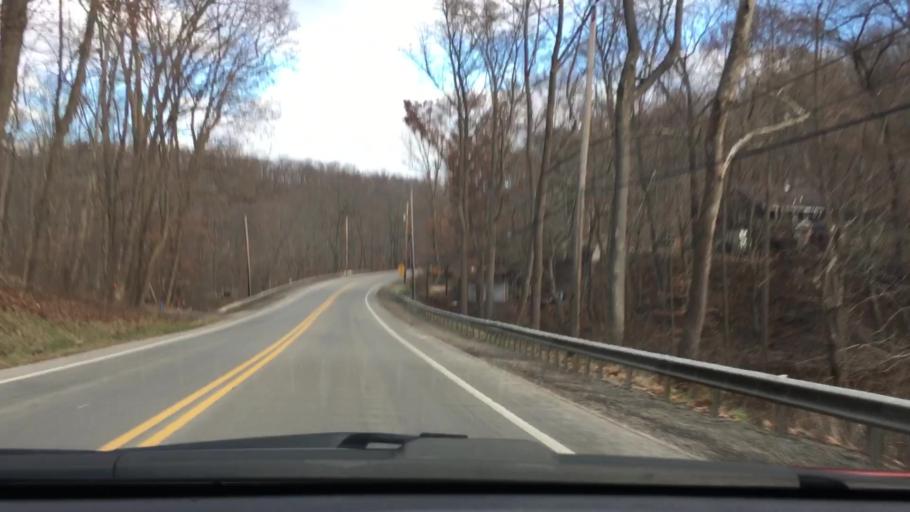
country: US
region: Pennsylvania
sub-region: Westmoreland County
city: Avonmore
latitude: 40.6244
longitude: -79.4291
